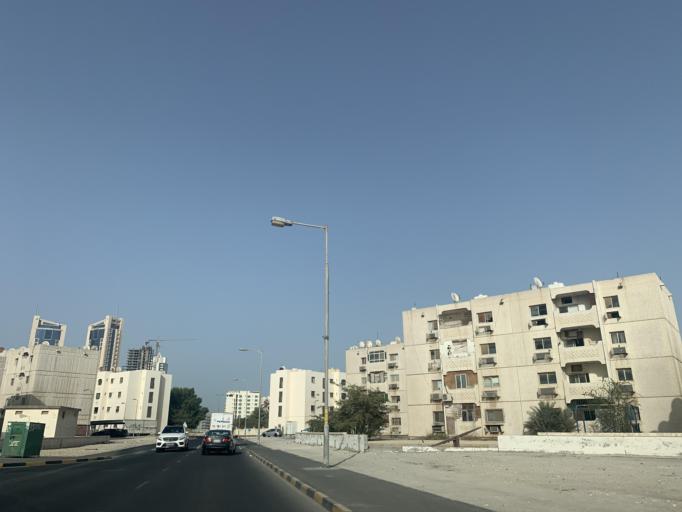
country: BH
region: Manama
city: Jidd Hafs
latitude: 26.2266
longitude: 50.5500
